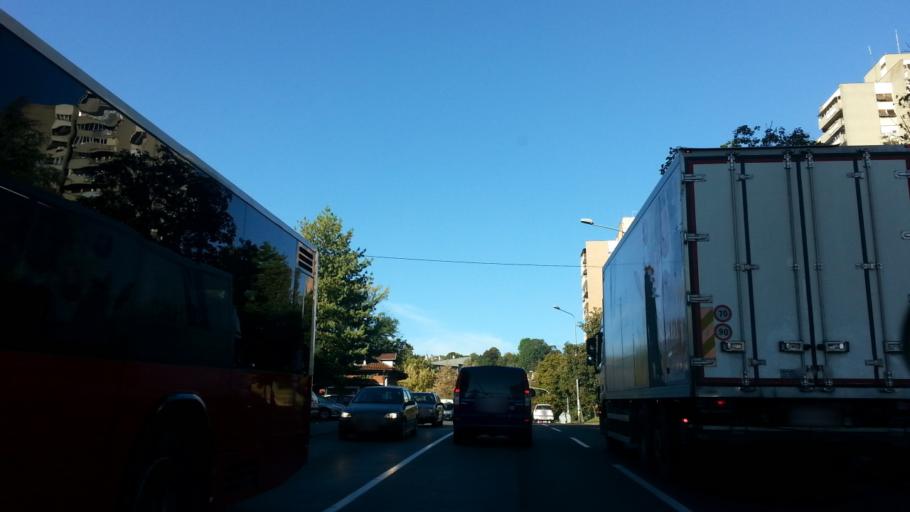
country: RS
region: Central Serbia
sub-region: Belgrade
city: Rakovica
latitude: 44.7452
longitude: 20.4361
